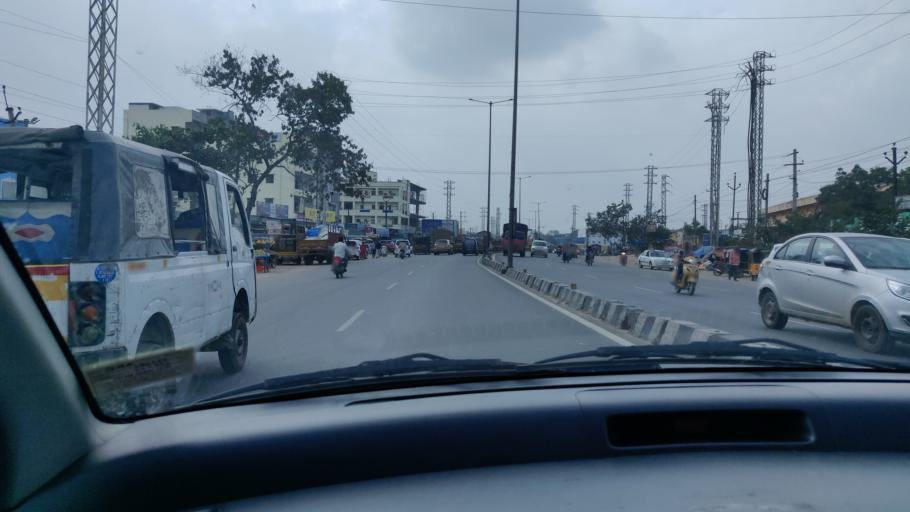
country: IN
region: Telangana
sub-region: Rangareddi
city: Balapur
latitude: 17.3148
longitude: 78.4461
